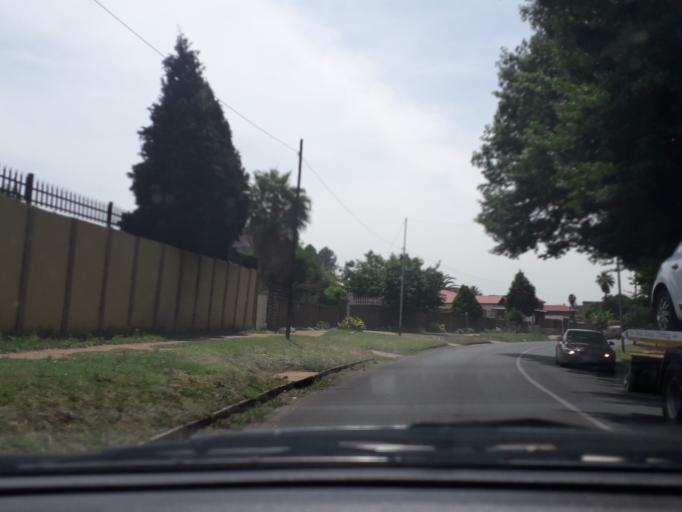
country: ZA
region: Gauteng
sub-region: City of Johannesburg Metropolitan Municipality
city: Roodepoort
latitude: -26.1810
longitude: 27.9297
